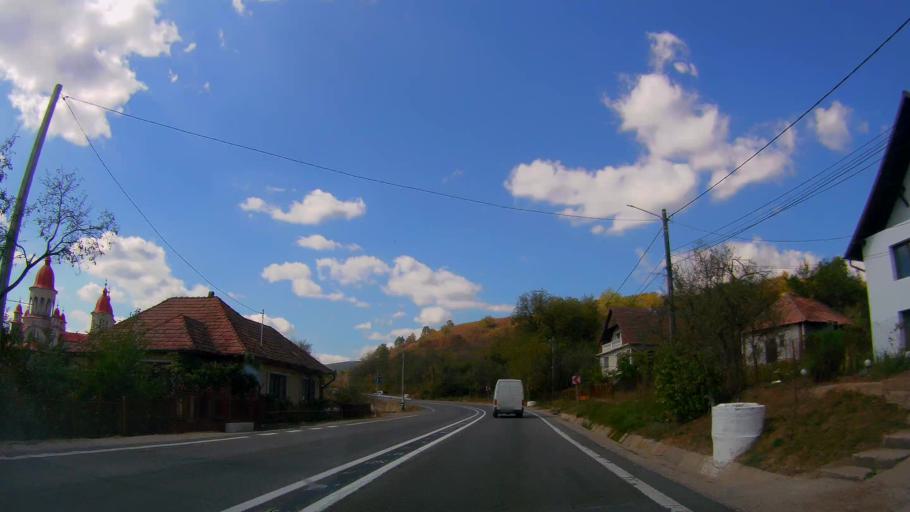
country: RO
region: Salaj
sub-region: Comuna Treznea
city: Treznea
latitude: 47.1240
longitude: 23.1371
